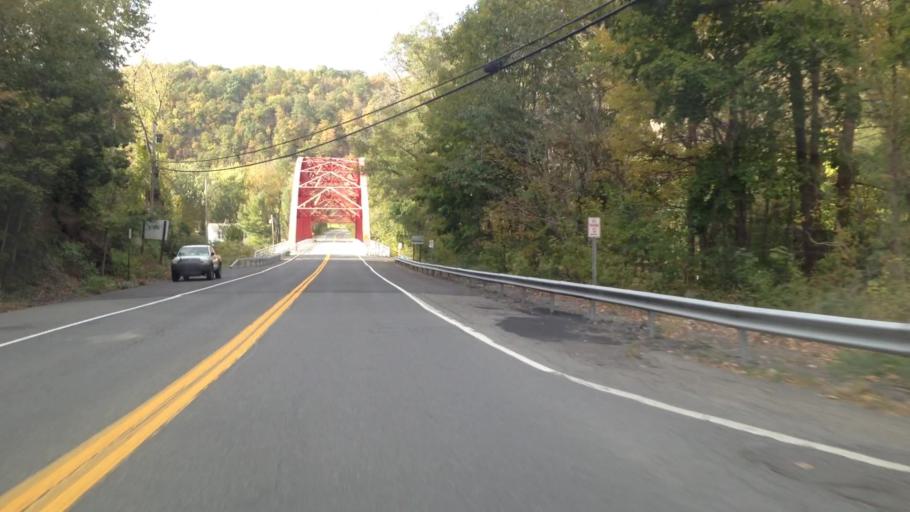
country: US
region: New York
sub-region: Ulster County
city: Kingston
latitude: 41.8935
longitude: -74.0175
